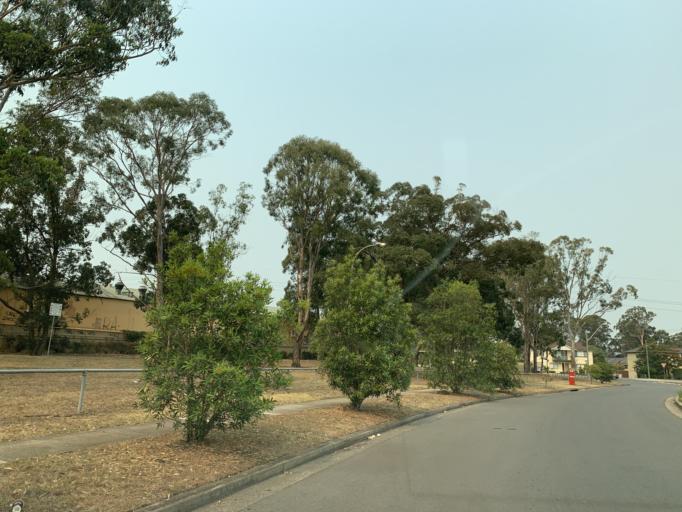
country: AU
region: New South Wales
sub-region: Holroyd
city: Girraween
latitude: -33.8001
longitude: 150.9258
